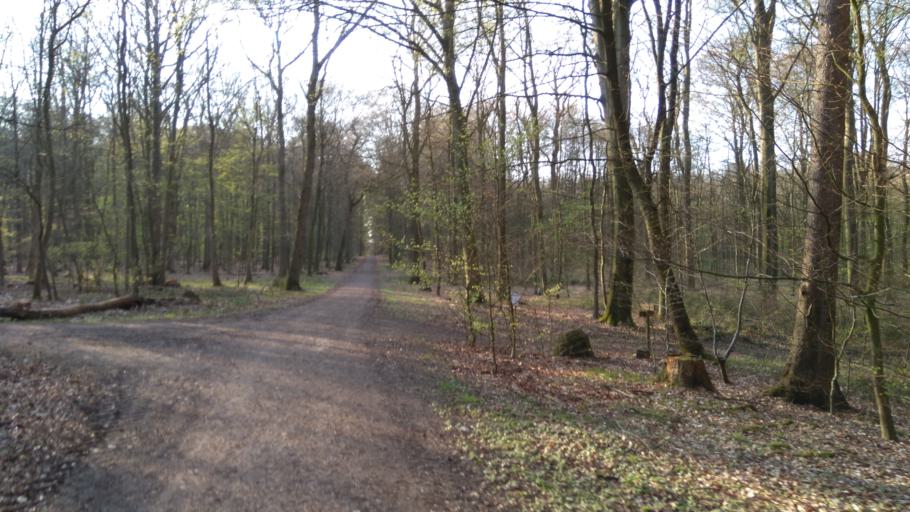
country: DE
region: Lower Saxony
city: Buxtehude
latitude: 53.4729
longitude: 9.6441
